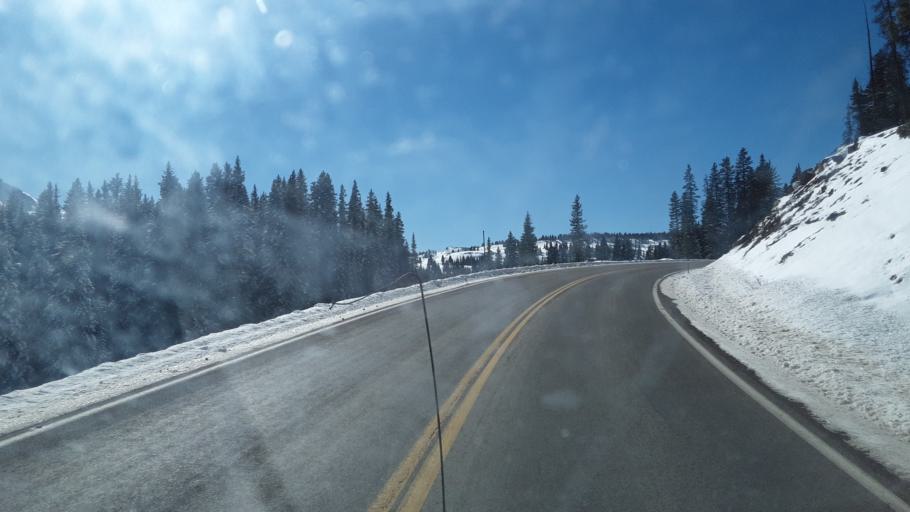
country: US
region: Colorado
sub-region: San Juan County
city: Silverton
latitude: 37.7489
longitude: -107.6861
